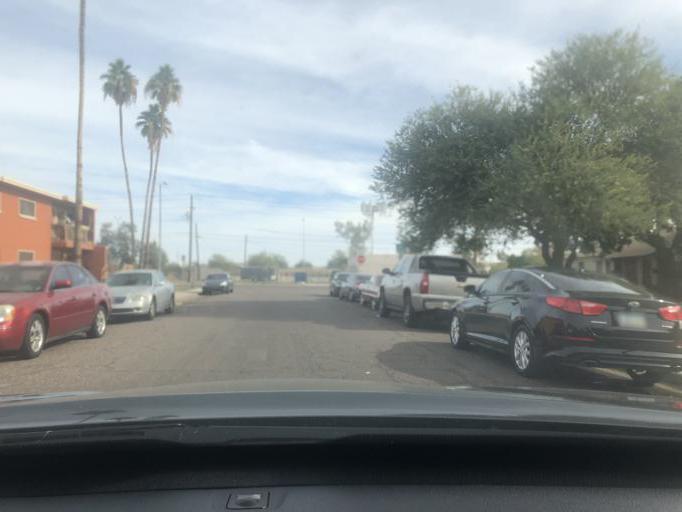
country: US
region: Arizona
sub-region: Maricopa County
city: Phoenix
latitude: 33.4562
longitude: -112.0397
